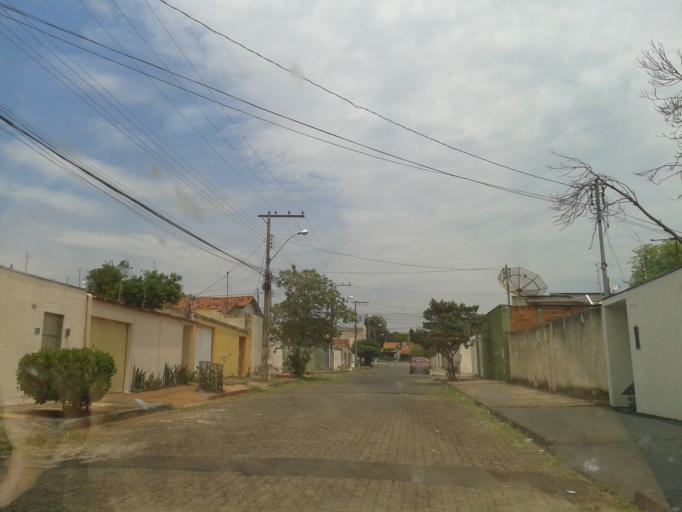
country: BR
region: Minas Gerais
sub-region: Uberlandia
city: Uberlandia
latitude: -18.9348
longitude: -48.3015
